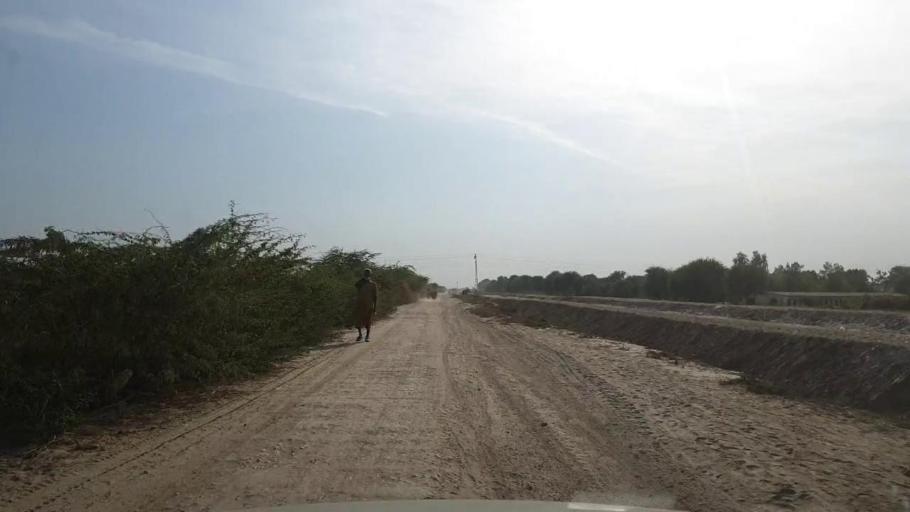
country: PK
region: Sindh
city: Kunri
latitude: 25.1649
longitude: 69.5215
